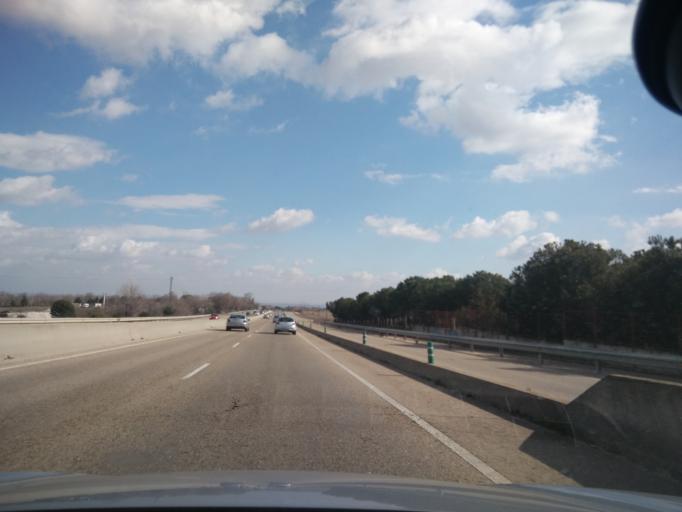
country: ES
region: Madrid
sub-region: Provincia de Madrid
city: Alcobendas
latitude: 40.5528
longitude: -3.6748
